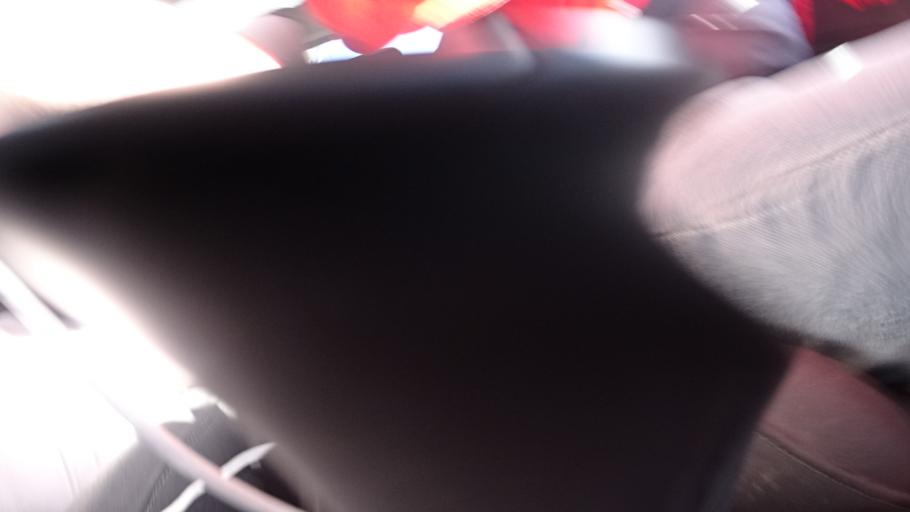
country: ES
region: Canary Islands
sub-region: Provincia de Las Palmas
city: Vega de San Mateo
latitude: 27.9642
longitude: -15.5476
